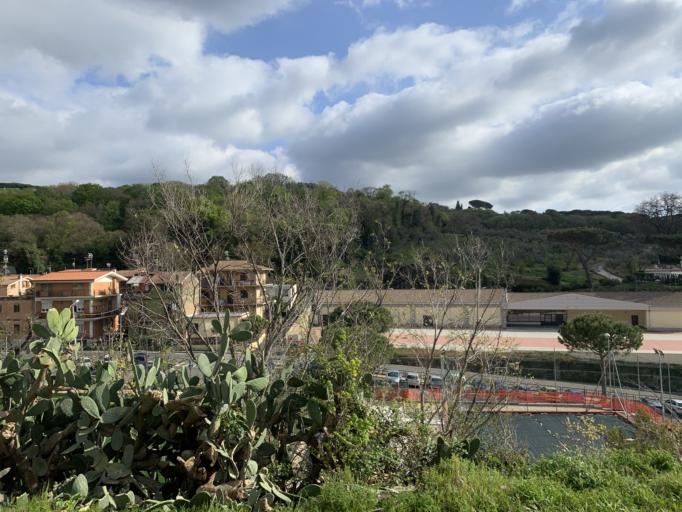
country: IT
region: Latium
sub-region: Citta metropolitana di Roma Capitale
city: Castel Gandolfo
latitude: 41.7691
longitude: 12.6532
